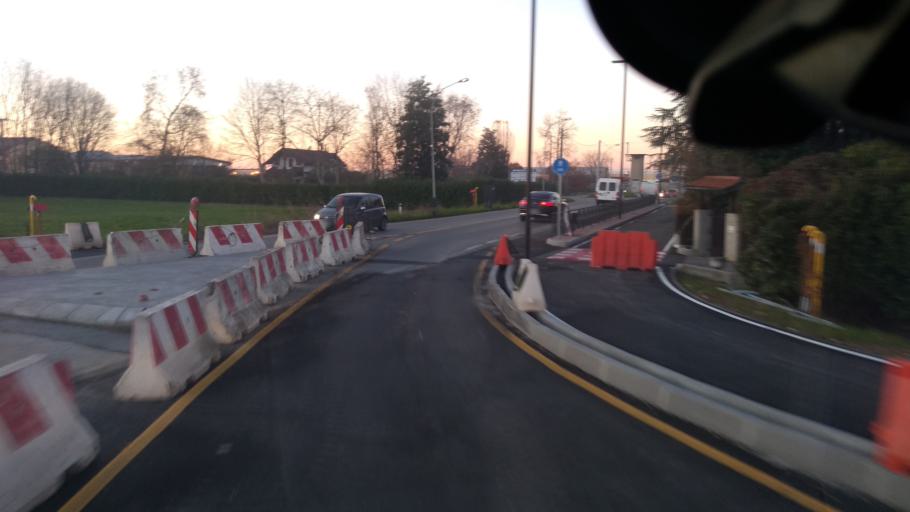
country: IT
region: Lombardy
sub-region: Provincia di Bergamo
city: Calvenzano
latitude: 45.5011
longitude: 9.5982
